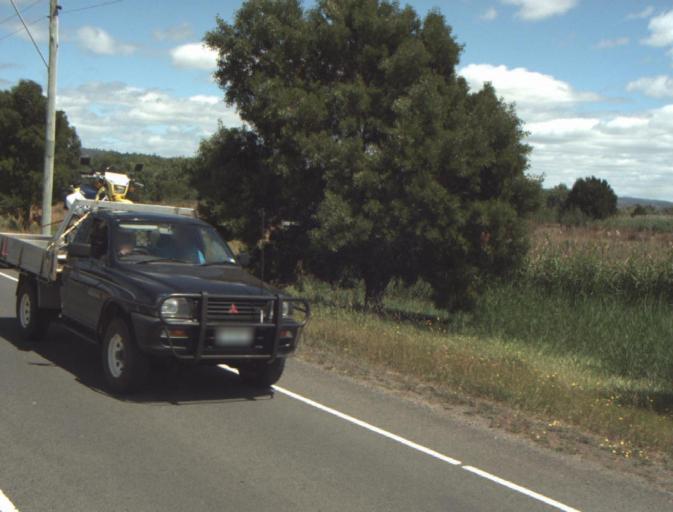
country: AU
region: Tasmania
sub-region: Launceston
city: Newstead
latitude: -41.4238
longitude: 147.1610
